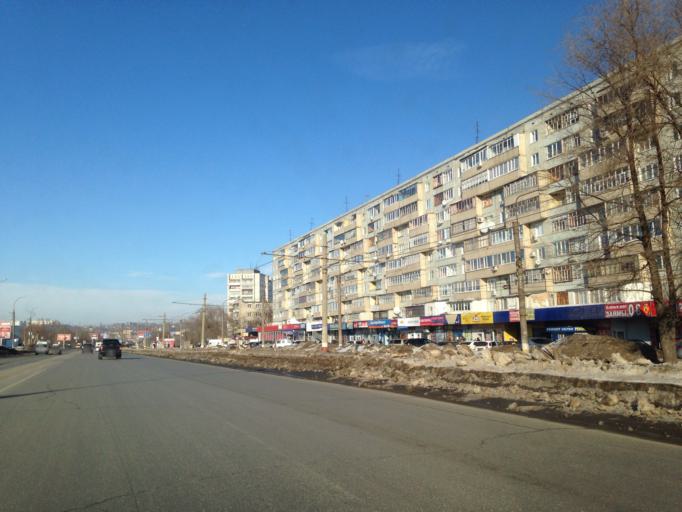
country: RU
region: Ulyanovsk
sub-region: Ulyanovskiy Rayon
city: Ulyanovsk
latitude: 54.3190
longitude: 48.3569
